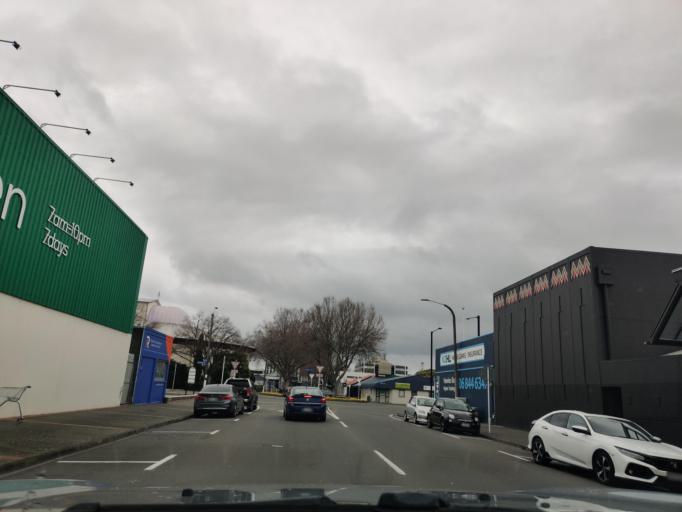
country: NZ
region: Hawke's Bay
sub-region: Napier City
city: Napier
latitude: -39.4934
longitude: 176.9135
